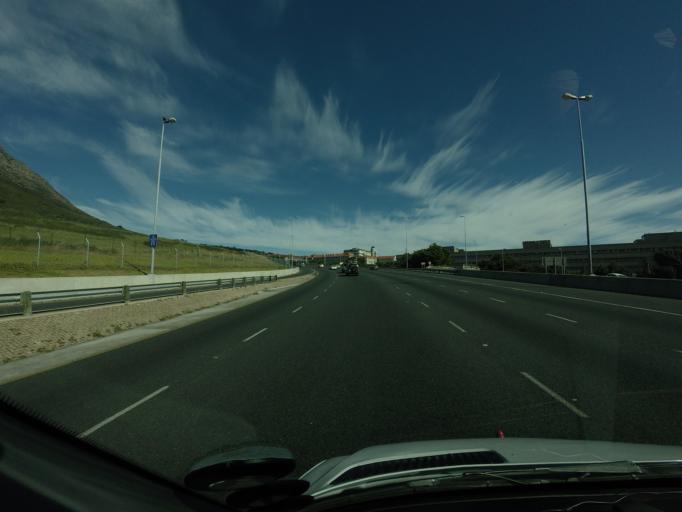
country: ZA
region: Western Cape
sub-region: City of Cape Town
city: Rosebank
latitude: -33.9441
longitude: 18.4649
